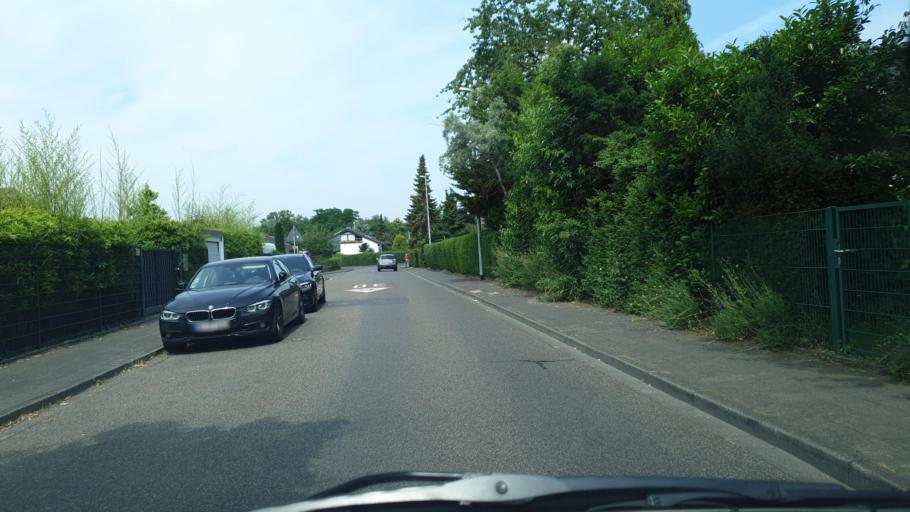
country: DE
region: North Rhine-Westphalia
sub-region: Regierungsbezirk Koln
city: Bergheim
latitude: 50.9377
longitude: 6.6701
